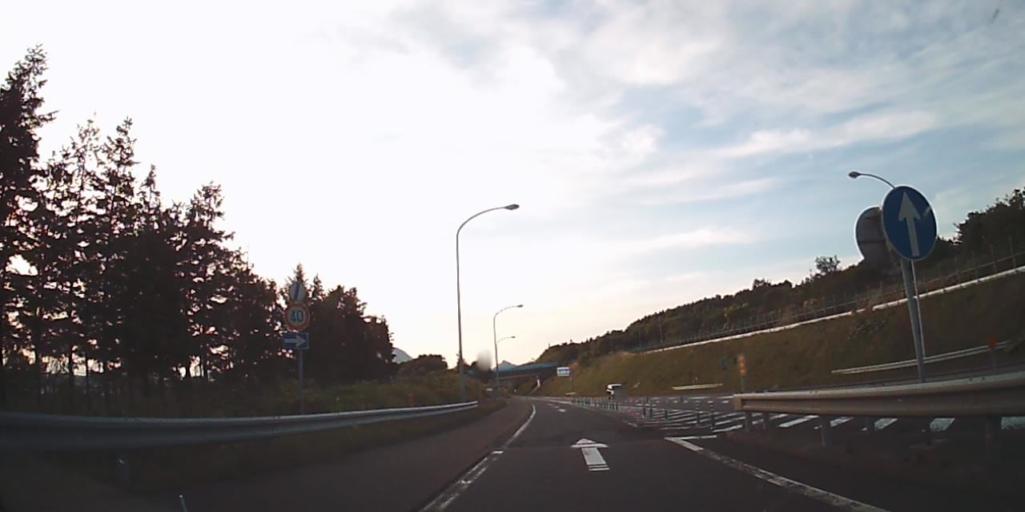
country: JP
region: Hokkaido
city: Date
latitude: 42.4681
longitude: 140.9071
